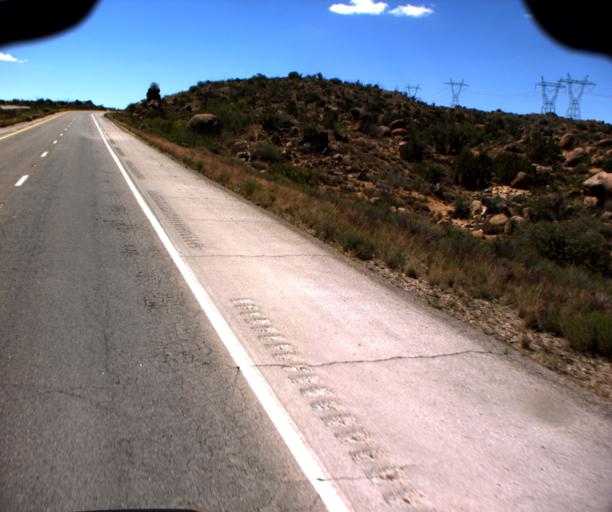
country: US
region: Arizona
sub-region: Yavapai County
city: Bagdad
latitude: 34.4637
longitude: -113.3001
